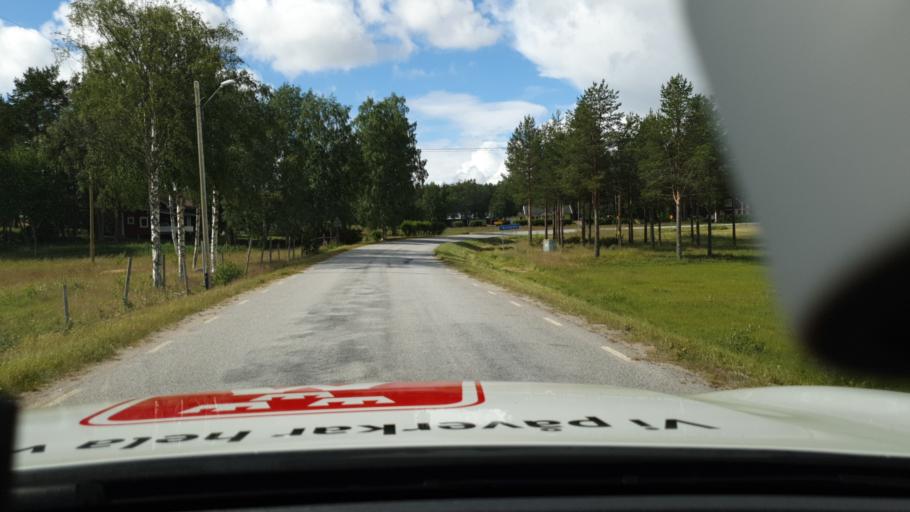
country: SE
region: Norrbotten
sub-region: Pitea Kommun
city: Rosvik
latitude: 65.3945
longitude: 21.7501
